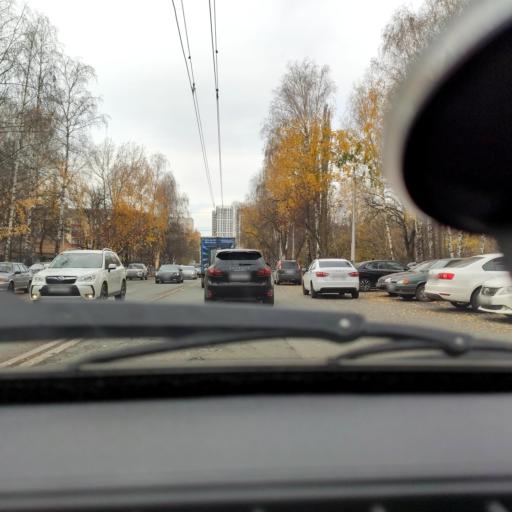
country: RU
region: Bashkortostan
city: Ufa
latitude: 54.7624
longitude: 56.0068
